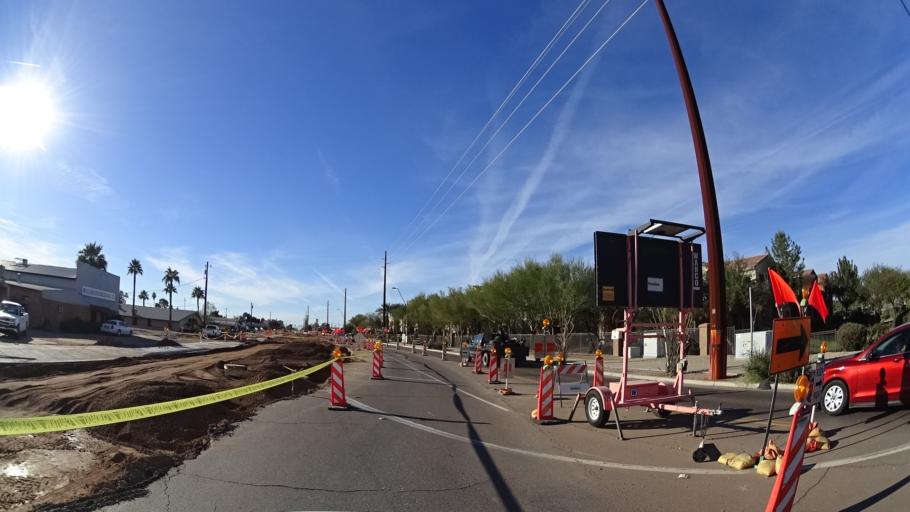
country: US
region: Arizona
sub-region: Maricopa County
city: Queen Creek
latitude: 33.2488
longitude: -111.6306
